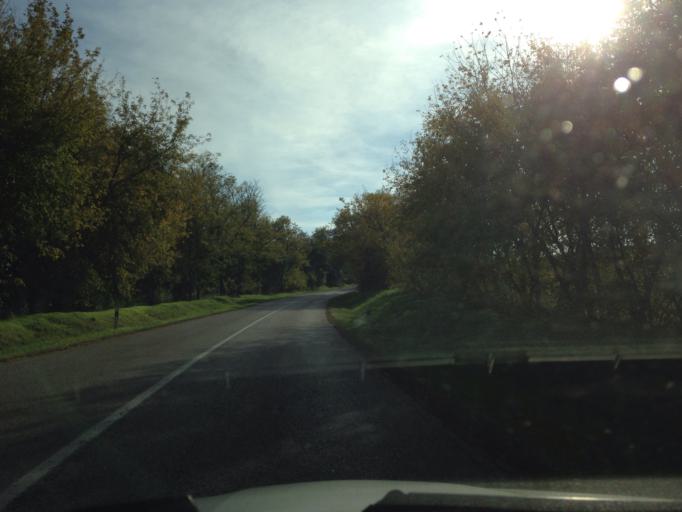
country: SK
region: Nitriansky
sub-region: Okres Komarno
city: Hurbanovo
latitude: 47.8769
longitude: 18.2860
